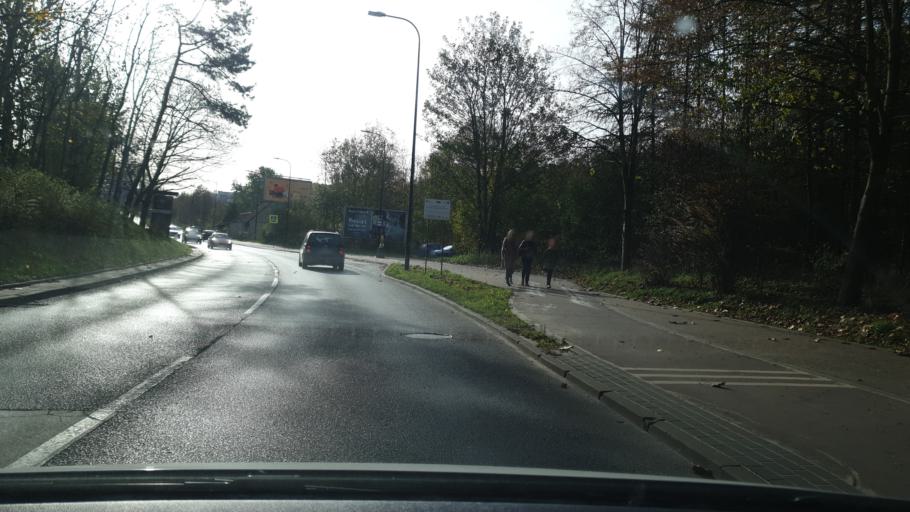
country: PL
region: Pomeranian Voivodeship
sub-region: Gdansk
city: Gdansk
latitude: 54.3659
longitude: 18.5892
